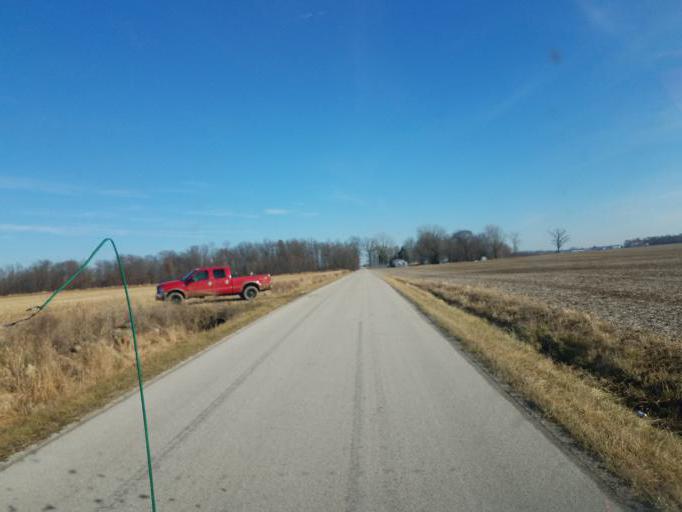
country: US
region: Ohio
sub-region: Morrow County
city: Cardington
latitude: 40.6016
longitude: -82.9325
